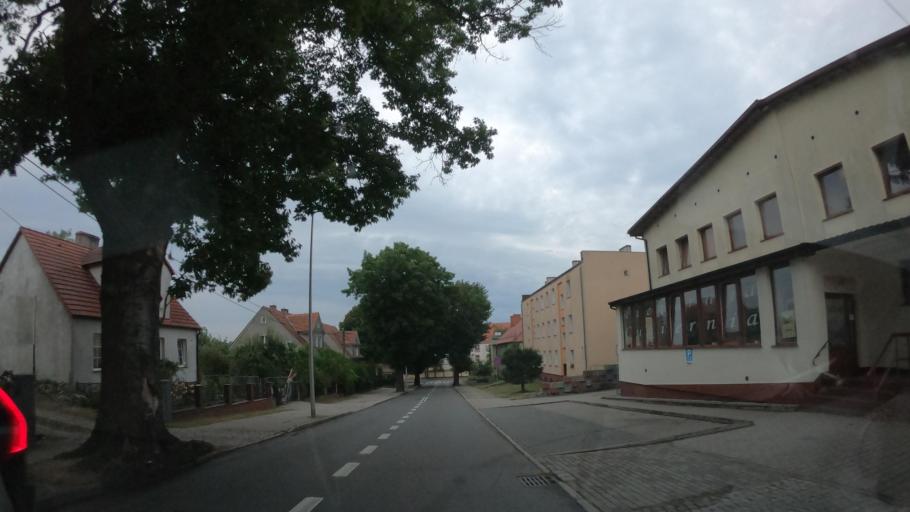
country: PL
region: Lubusz
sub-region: Powiat krosnienski
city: Krosno Odrzanskie
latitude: 52.0568
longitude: 15.1119
